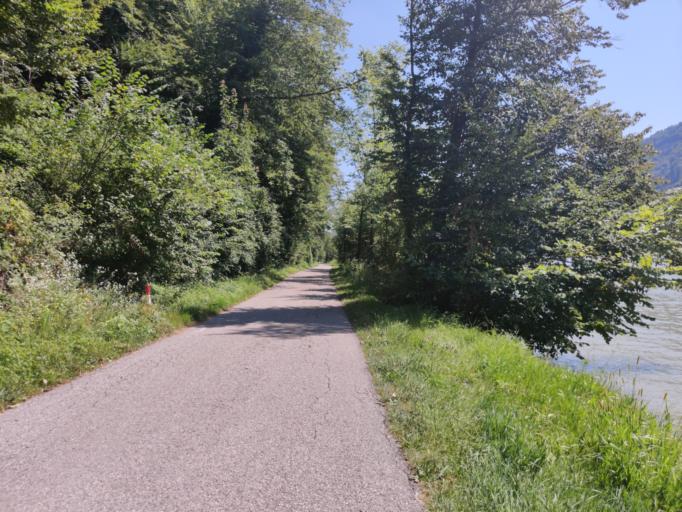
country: AT
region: Upper Austria
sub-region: Politischer Bezirk Rohrbach
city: Pfarrkirchen im Muehlkreis
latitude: 48.4372
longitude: 13.8463
